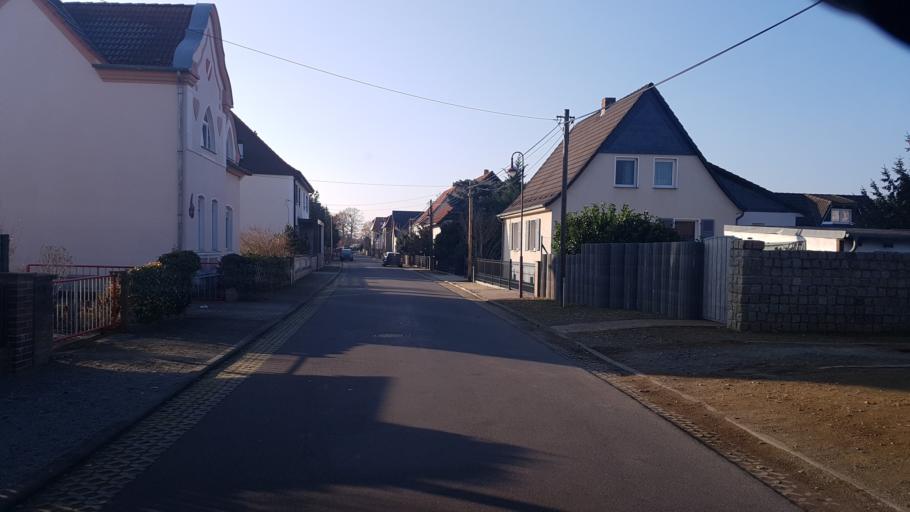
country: DE
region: Brandenburg
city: Lauchhammer
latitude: 51.4706
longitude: 13.7481
